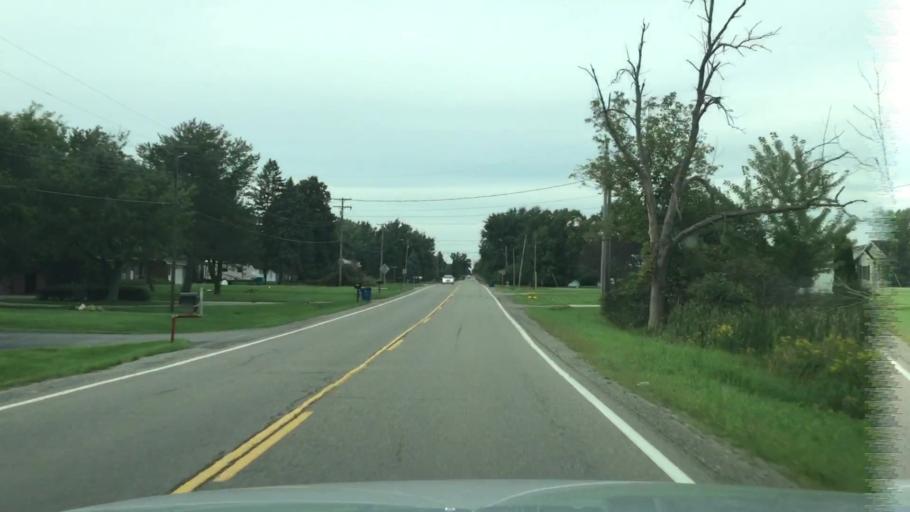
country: US
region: Michigan
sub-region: Genesee County
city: Linden
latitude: 42.8727
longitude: -83.7686
